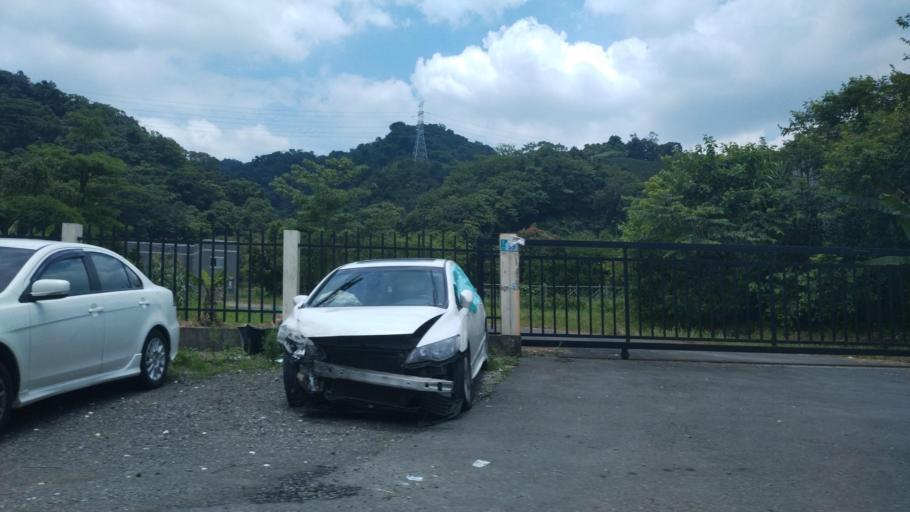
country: TW
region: Taipei
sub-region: Taipei
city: Banqiao
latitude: 24.9318
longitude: 121.4541
